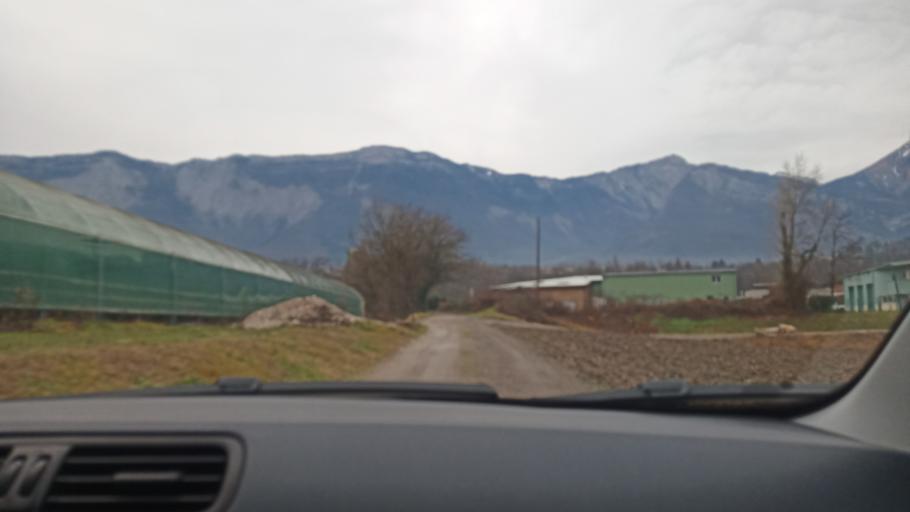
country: FR
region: Rhone-Alpes
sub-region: Departement de l'Isere
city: Saint-Nazaire-les-Eymes
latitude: 45.2397
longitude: 5.8560
